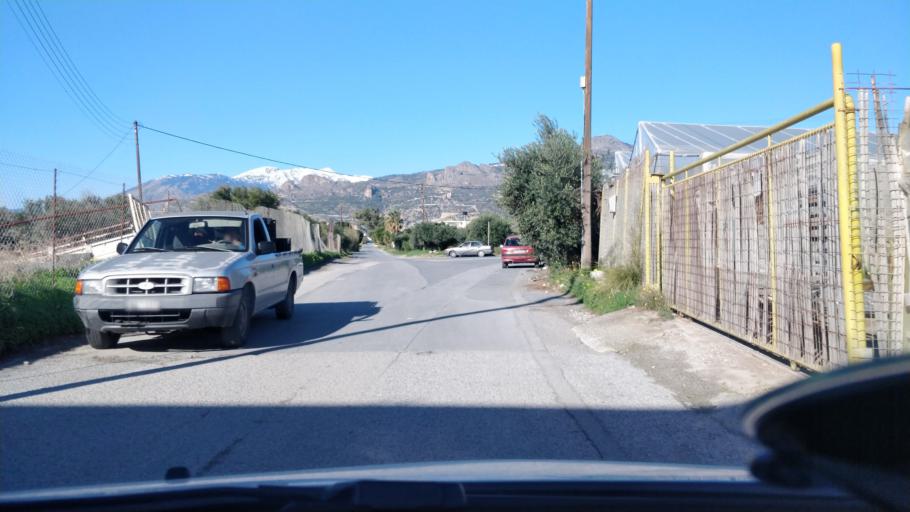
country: GR
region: Crete
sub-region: Nomos Lasithiou
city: Gra Liyia
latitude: 35.0169
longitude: 25.6892
